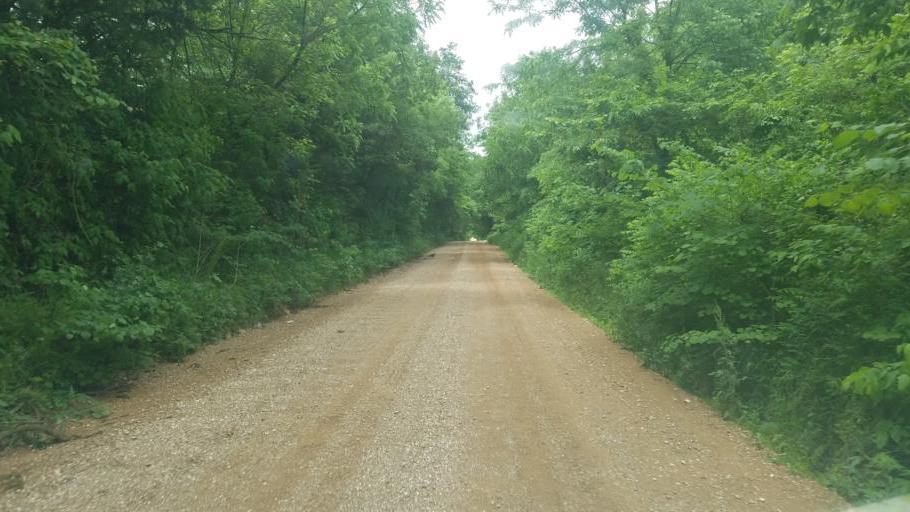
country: US
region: Missouri
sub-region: Moniteau County
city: California
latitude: 38.6236
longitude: -92.6190
